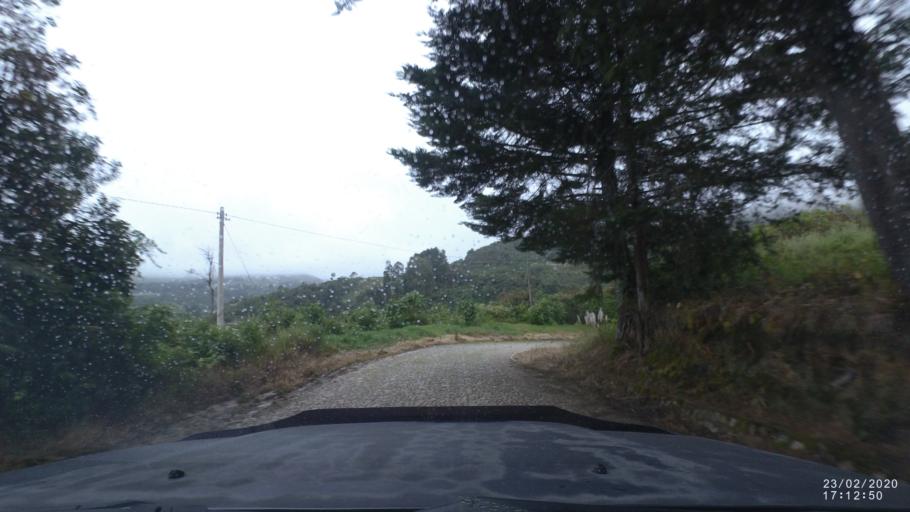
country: BO
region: Cochabamba
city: Colomi
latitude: -17.1361
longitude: -65.9424
